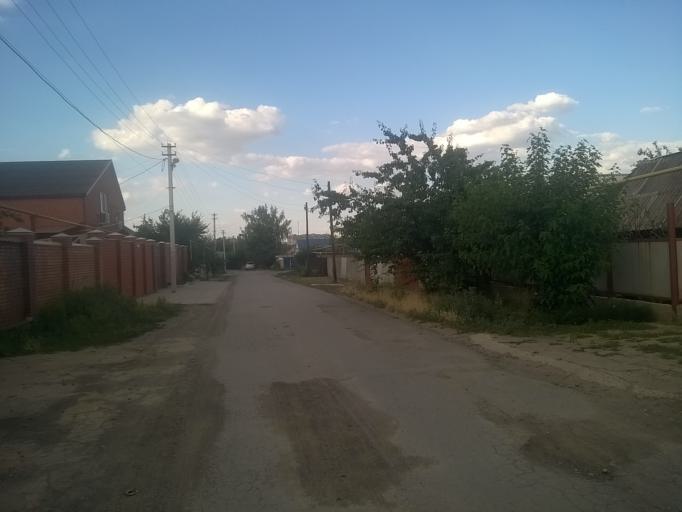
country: RU
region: Rostov
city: Donetsk
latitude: 48.3396
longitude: 39.9586
